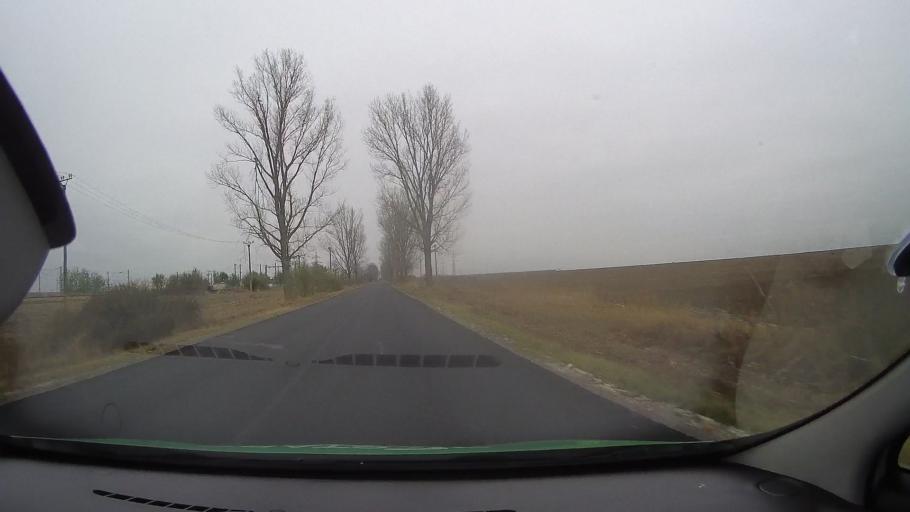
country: RO
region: Ialomita
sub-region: Comuna Valea Ciorii
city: Valea Ciorii
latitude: 44.7497
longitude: 27.5695
